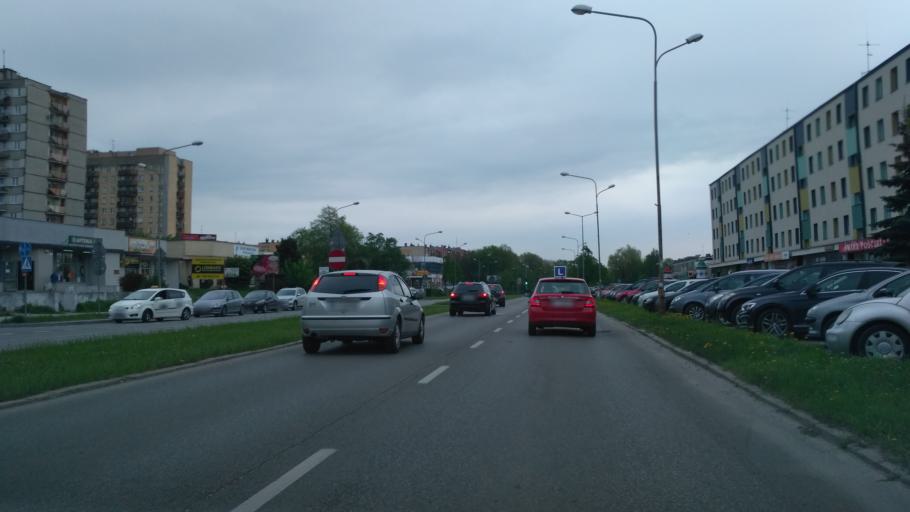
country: PL
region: Lesser Poland Voivodeship
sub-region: Powiat tarnowski
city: Tarnow
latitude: 50.0175
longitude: 21.0029
